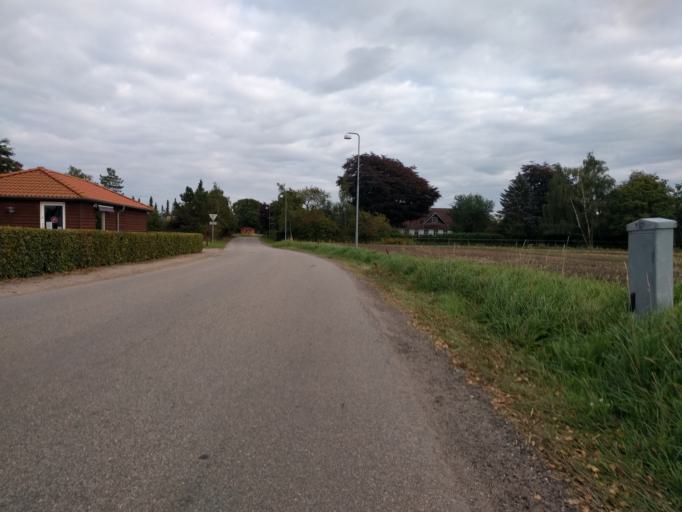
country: DK
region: South Denmark
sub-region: Odense Kommune
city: Bullerup
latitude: 55.4372
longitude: 10.5065
